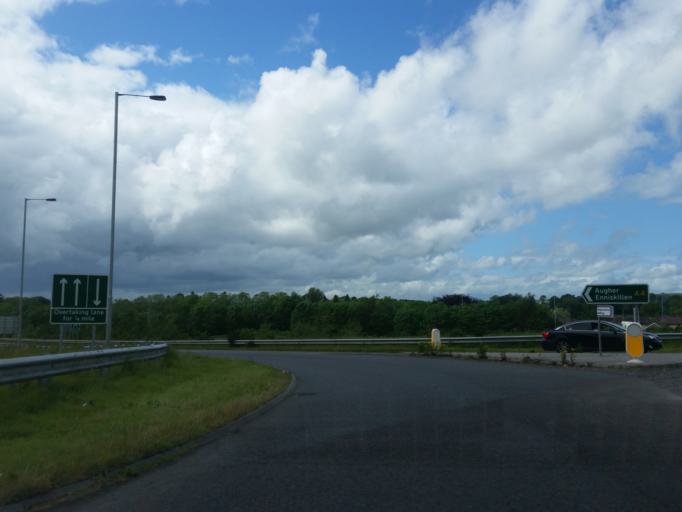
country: IE
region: Ulster
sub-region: County Monaghan
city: Monaghan
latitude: 54.4548
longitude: -7.0326
